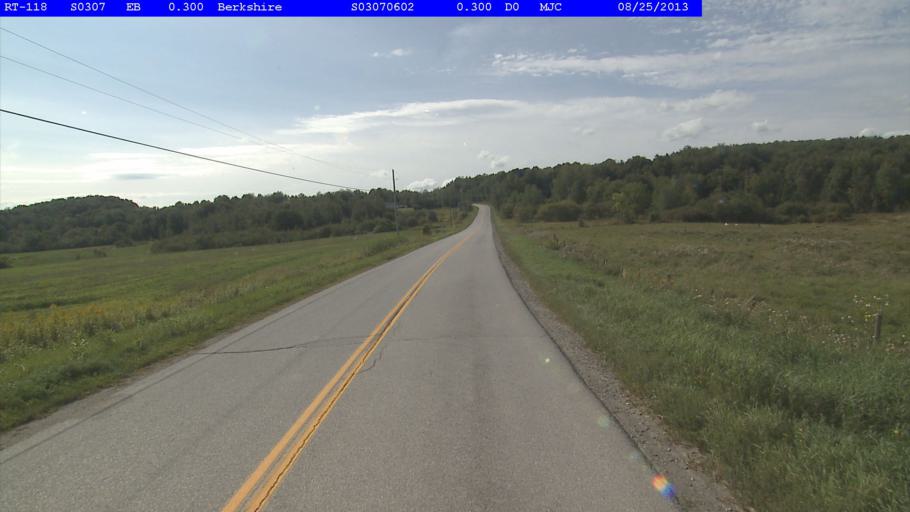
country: US
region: Vermont
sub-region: Franklin County
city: Richford
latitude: 44.9343
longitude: -72.7175
